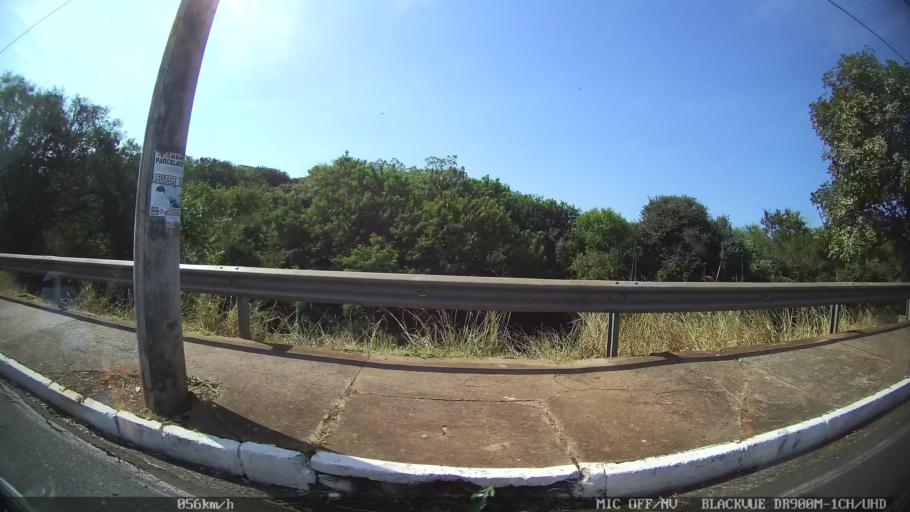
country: BR
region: Sao Paulo
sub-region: Sao Jose Do Rio Preto
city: Sao Jose do Rio Preto
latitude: -20.7983
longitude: -49.3990
